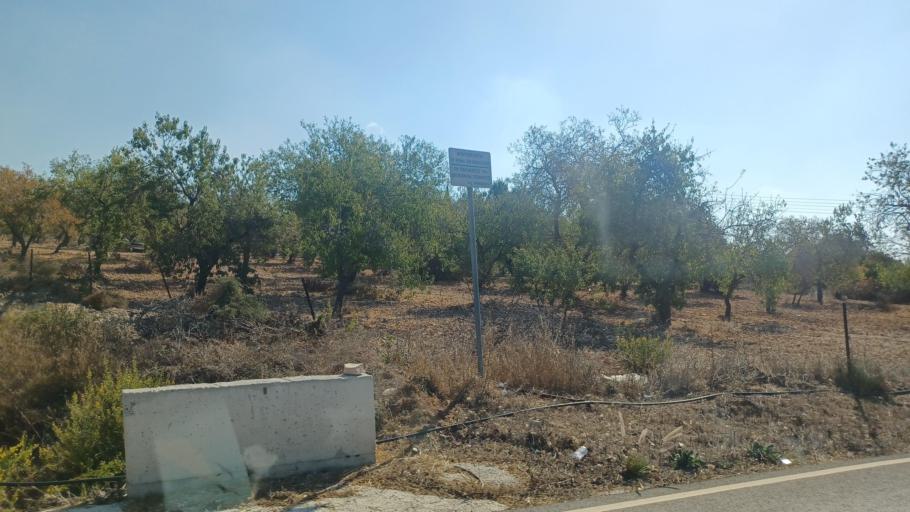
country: CY
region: Pafos
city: Mesogi
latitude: 34.8283
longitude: 32.4464
